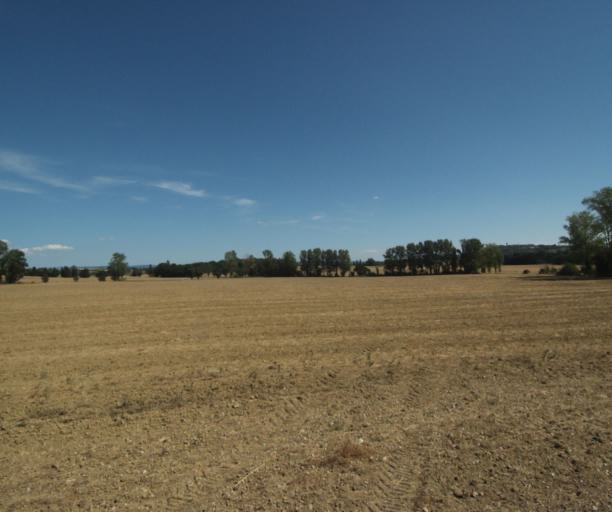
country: FR
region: Midi-Pyrenees
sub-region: Departement de la Haute-Garonne
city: Saint-Felix-Lauragais
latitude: 43.5146
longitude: 1.8930
